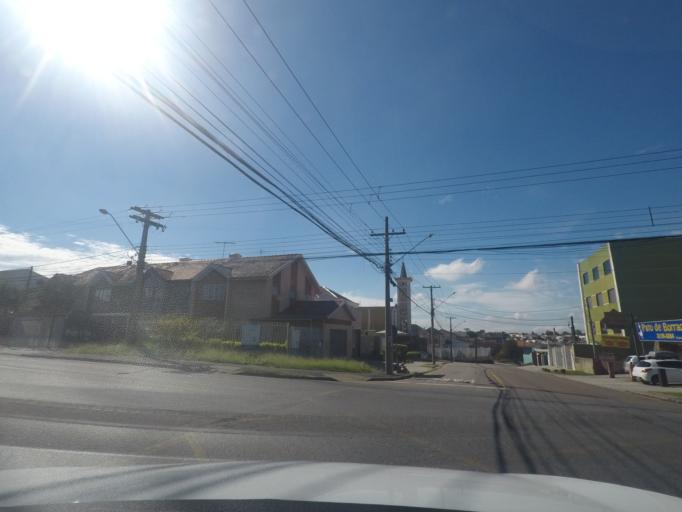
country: BR
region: Parana
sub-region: Sao Jose Dos Pinhais
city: Sao Jose dos Pinhais
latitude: -25.5051
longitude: -49.2737
